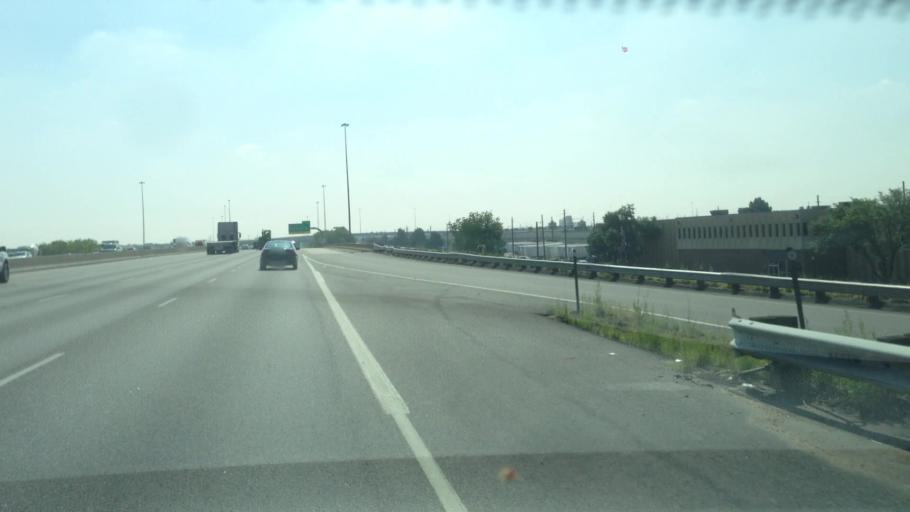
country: US
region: Colorado
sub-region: Adams County
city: Aurora
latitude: 39.7737
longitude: -104.8434
